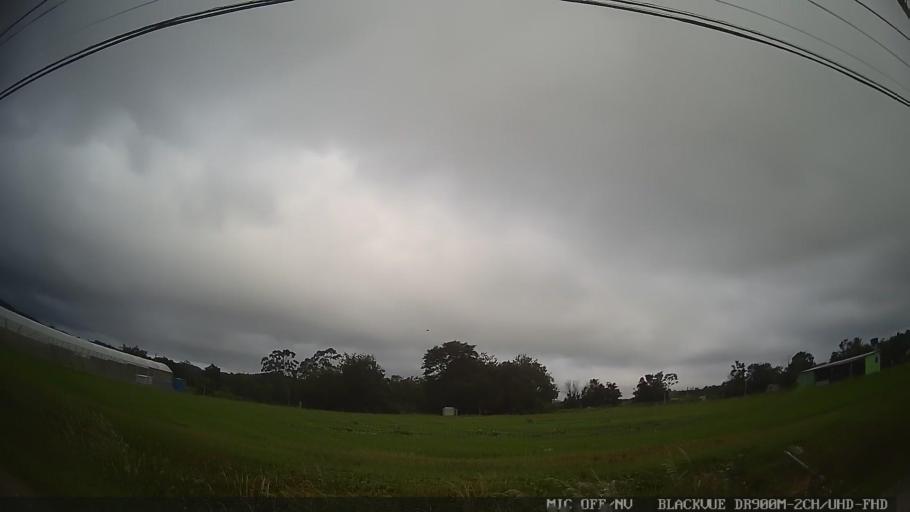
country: BR
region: Sao Paulo
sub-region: Biritiba-Mirim
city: Biritiba Mirim
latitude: -23.5565
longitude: -46.0861
